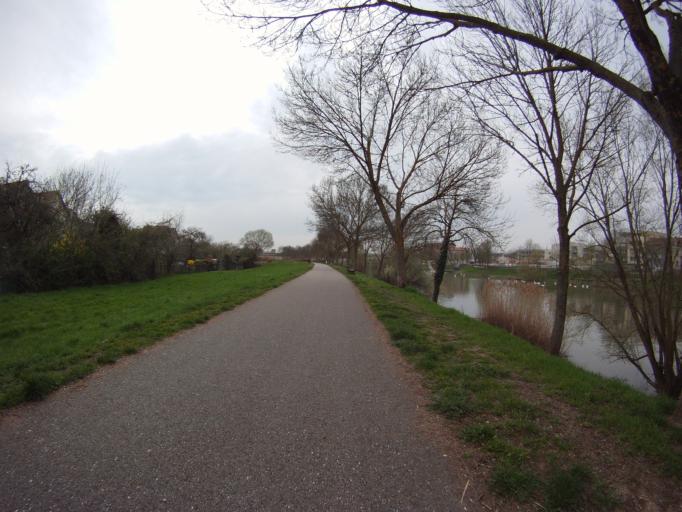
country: FR
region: Lorraine
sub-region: Departement de Meurthe-et-Moselle
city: Malzeville
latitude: 48.7076
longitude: 6.1816
